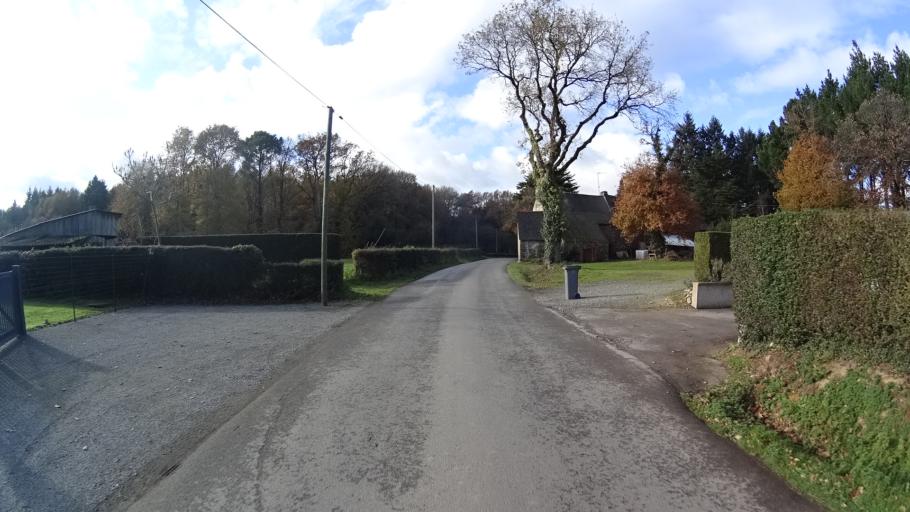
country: FR
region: Brittany
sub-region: Departement du Morbihan
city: Carentoir
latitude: 47.8237
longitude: -2.0958
